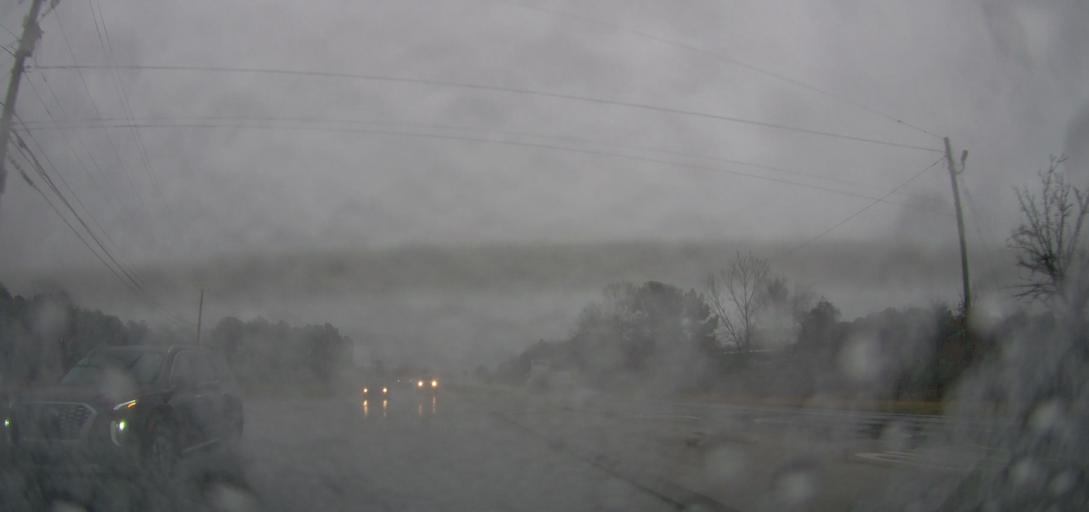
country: US
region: Alabama
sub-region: Elmore County
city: Millbrook
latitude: 32.3991
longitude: -86.3984
